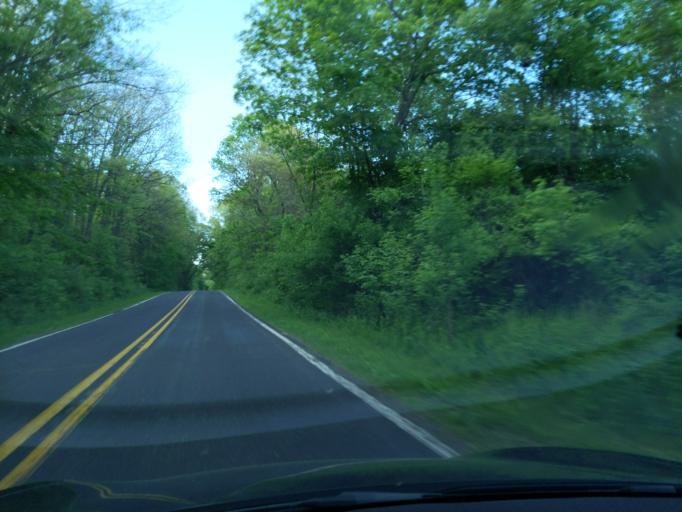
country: US
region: Michigan
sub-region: Ingham County
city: Stockbridge
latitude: 42.5174
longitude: -84.3054
